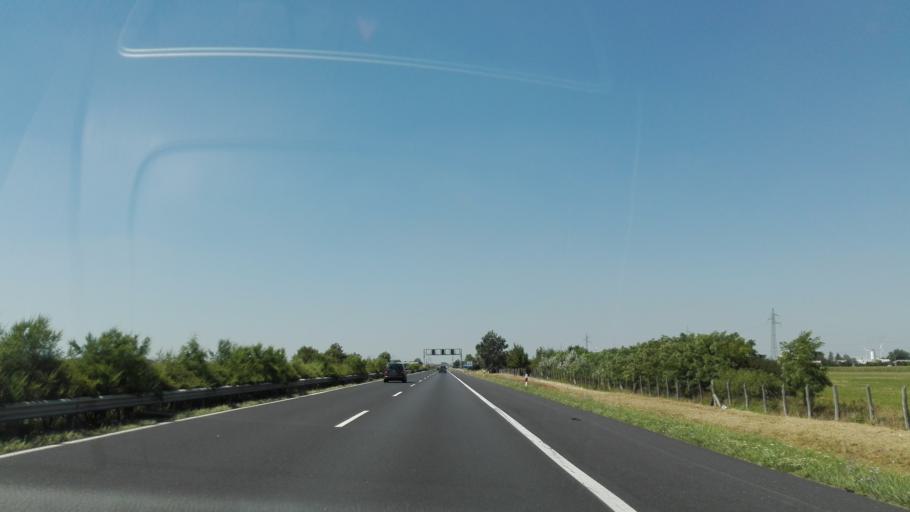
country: HU
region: Gyor-Moson-Sopron
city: Mosonmagyarovar
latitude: 47.8390
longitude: 17.2660
